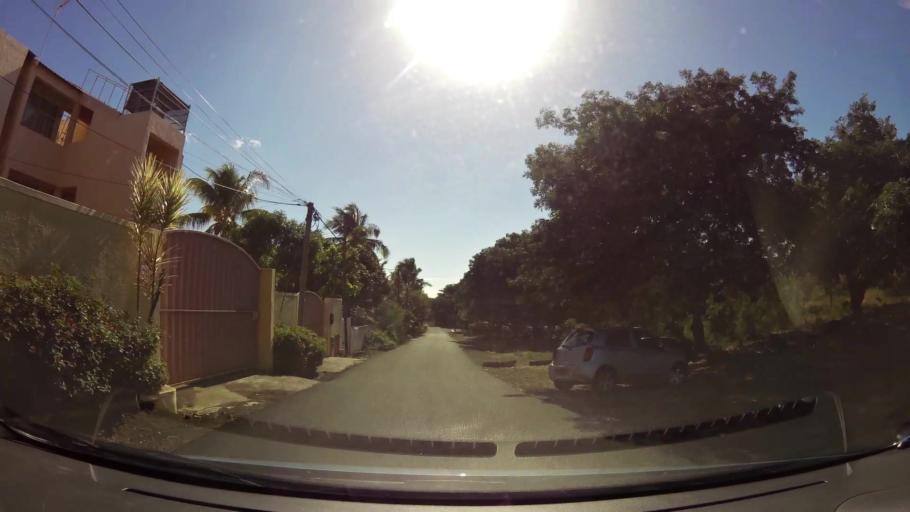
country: MU
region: Black River
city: Flic en Flac
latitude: -20.2677
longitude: 57.3753
